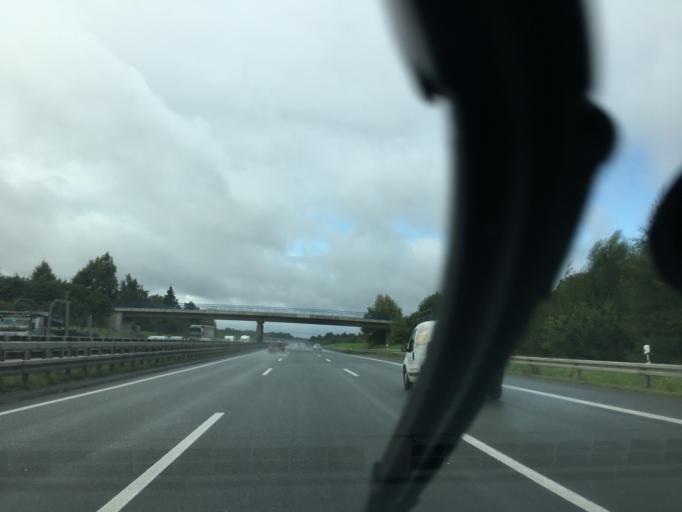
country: DE
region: North Rhine-Westphalia
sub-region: Regierungsbezirk Arnsberg
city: Welver
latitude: 51.6653
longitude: 7.9296
